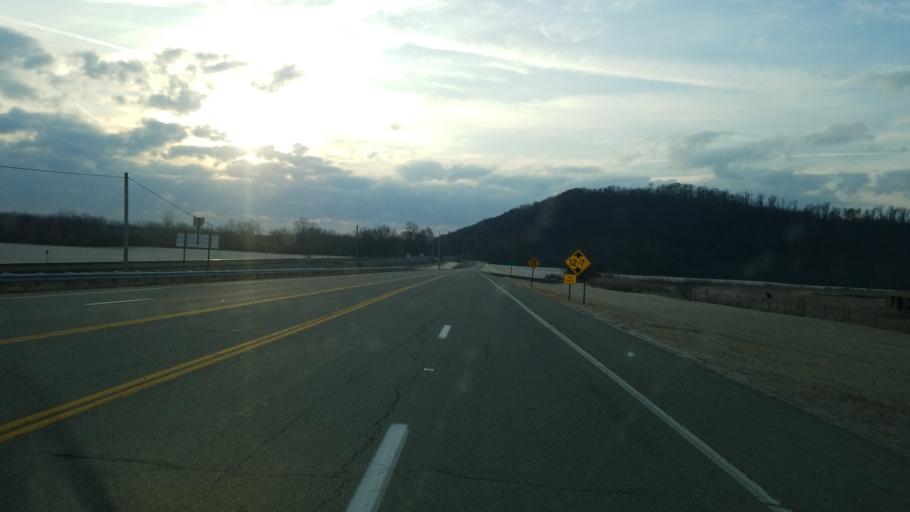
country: US
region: Ohio
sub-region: Ross County
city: Chillicothe
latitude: 39.2898
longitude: -82.9430
